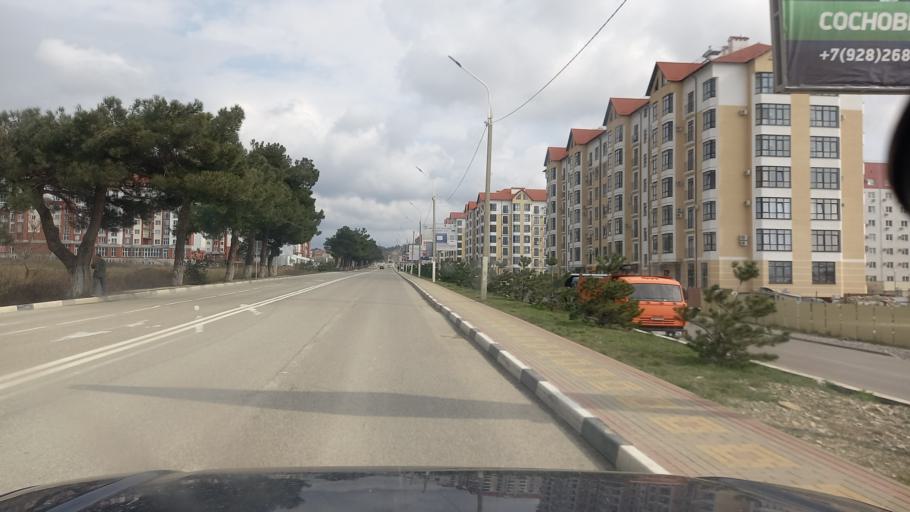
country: RU
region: Krasnodarskiy
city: Gelendzhik
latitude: 44.5577
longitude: 38.1019
